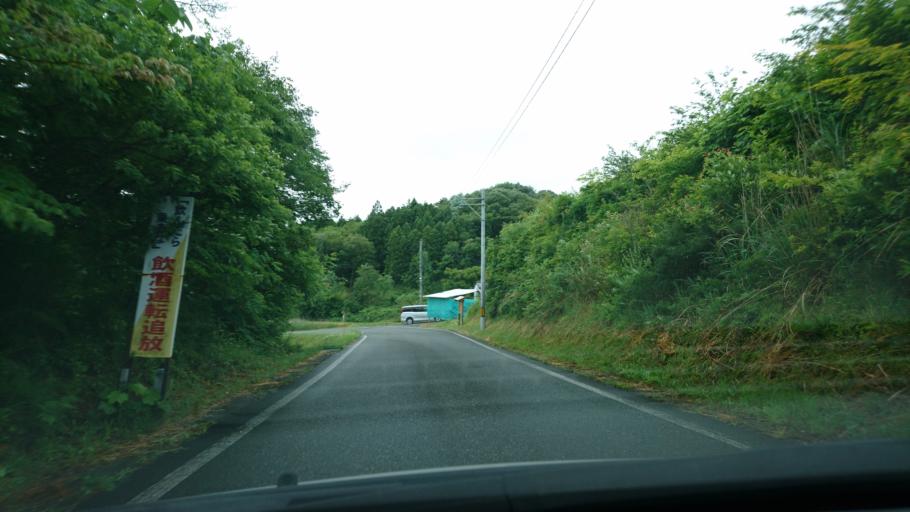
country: JP
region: Iwate
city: Ichinoseki
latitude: 38.8983
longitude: 141.1445
